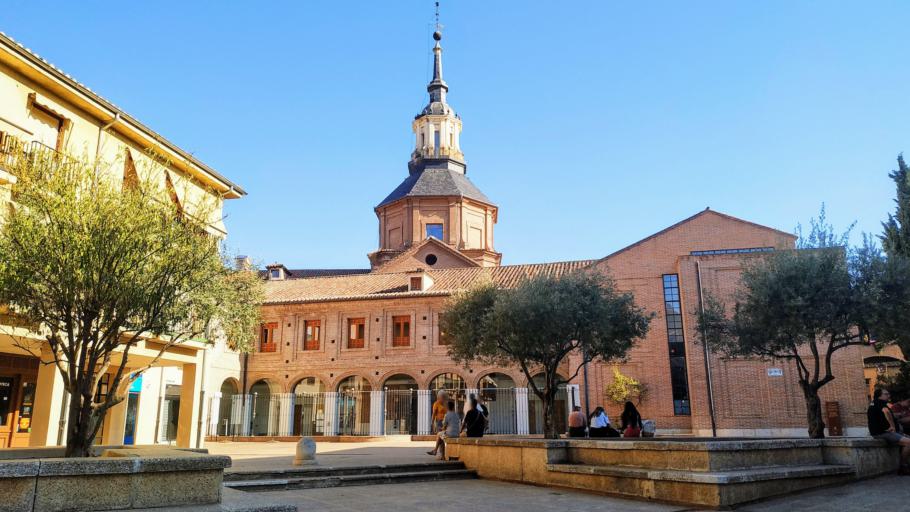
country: ES
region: Madrid
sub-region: Provincia de Madrid
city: Alcala de Henares
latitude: 40.4816
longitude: -3.3667
